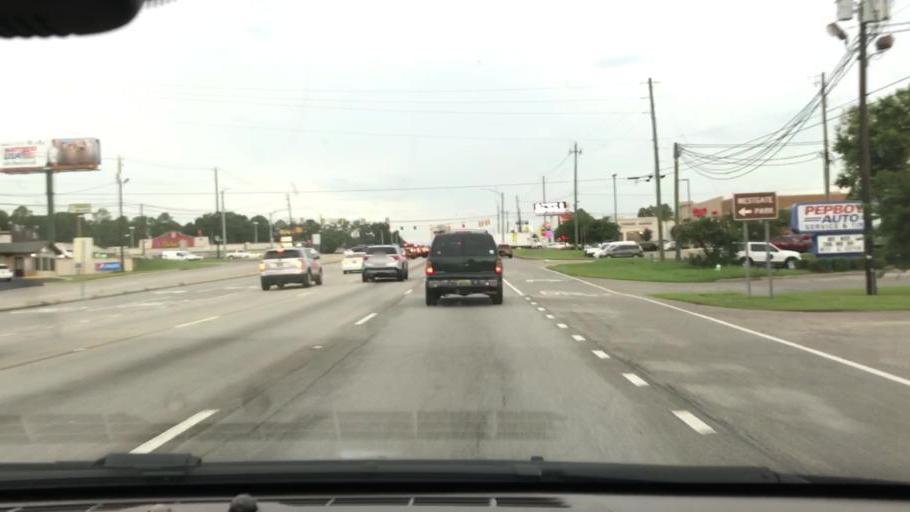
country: US
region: Alabama
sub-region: Houston County
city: Dothan
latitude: 31.2561
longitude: -85.4320
